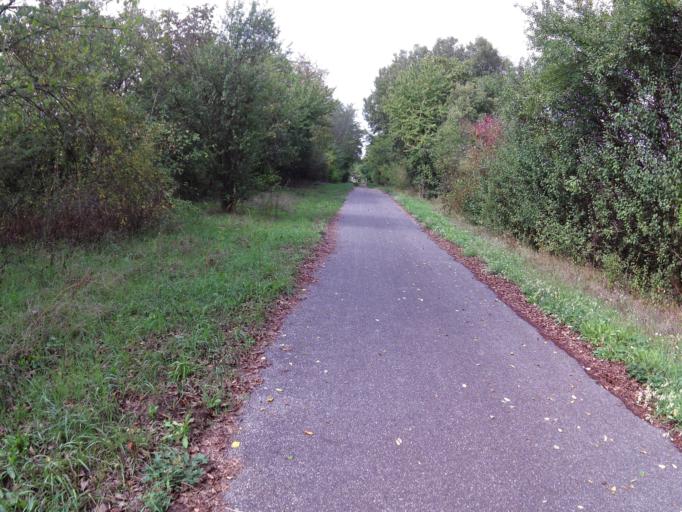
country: FR
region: Alsace
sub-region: Departement du Haut-Rhin
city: Kunheim
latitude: 48.0687
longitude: 7.5364
